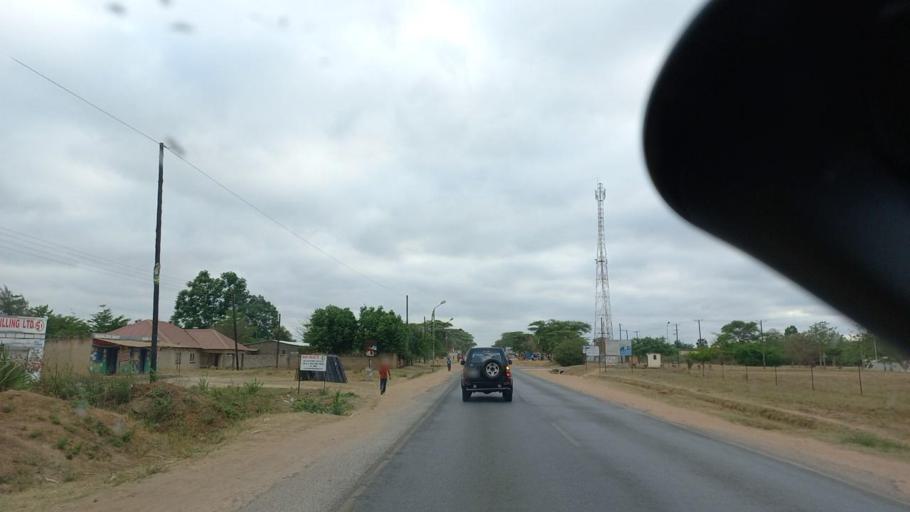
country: ZM
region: Lusaka
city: Chongwe
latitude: -15.3392
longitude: 28.6667
